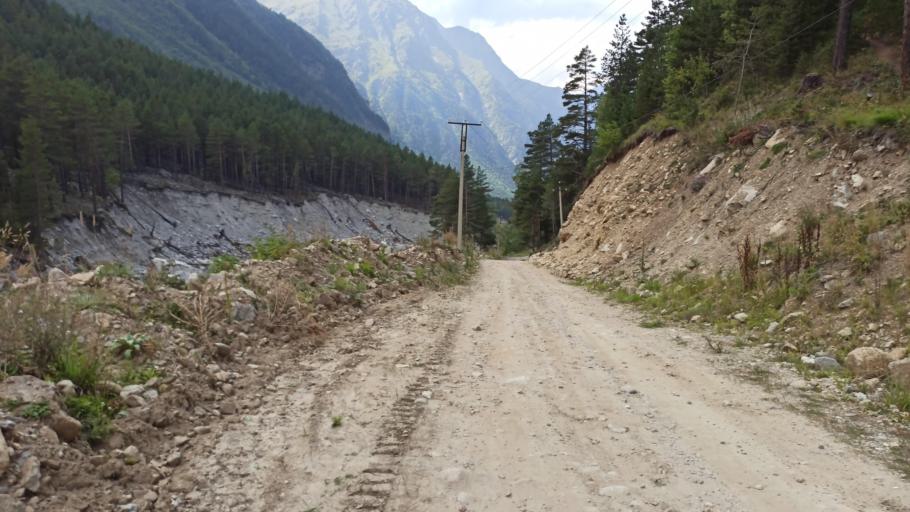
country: RU
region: Kabardino-Balkariya
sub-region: El'brusskiy Rayon
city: El'brus
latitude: 43.2195
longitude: 42.6903
